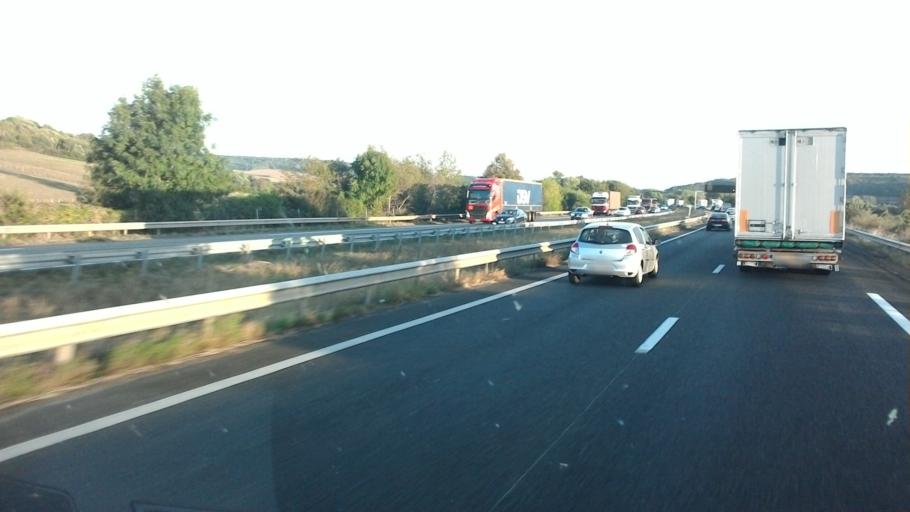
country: FR
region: Lorraine
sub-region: Departement de Meurthe-et-Moselle
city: Belleville
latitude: 48.8322
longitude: 6.0930
